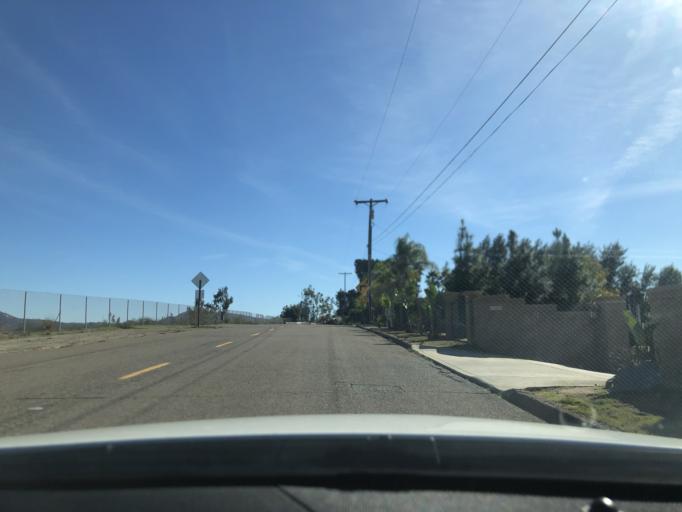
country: US
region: California
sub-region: San Diego County
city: Escondido
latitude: 33.0874
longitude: -117.0784
